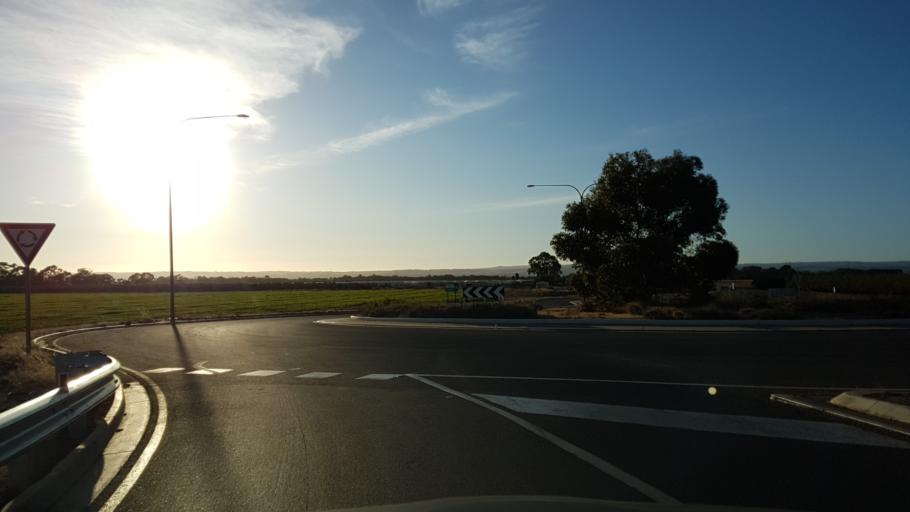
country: AU
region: South Australia
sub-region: Playford
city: Virginia
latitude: -34.6852
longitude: 138.6017
